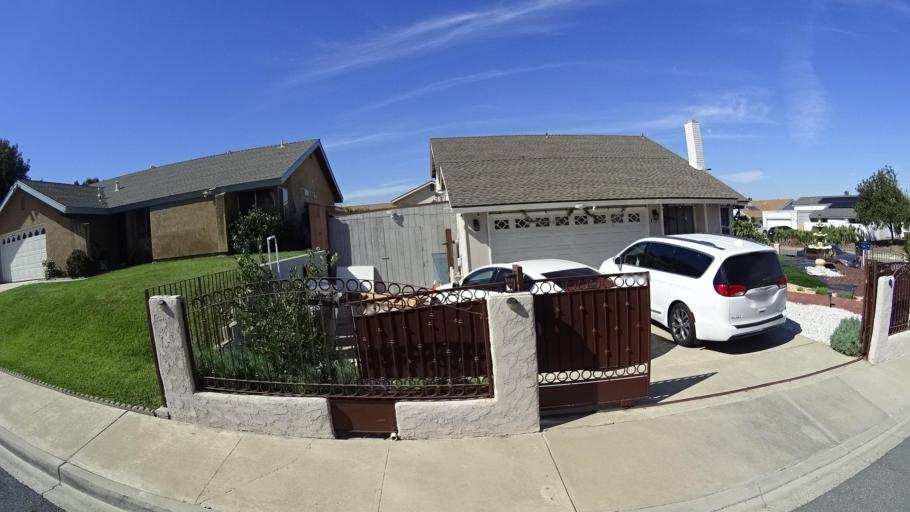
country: US
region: California
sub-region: San Diego County
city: La Presa
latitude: 32.7053
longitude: -117.0039
